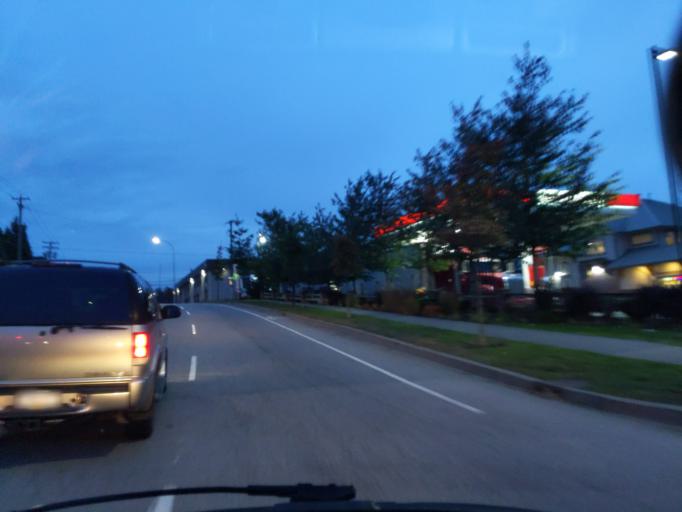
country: CA
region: British Columbia
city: Pitt Meadows
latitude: 49.1770
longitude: -122.6904
